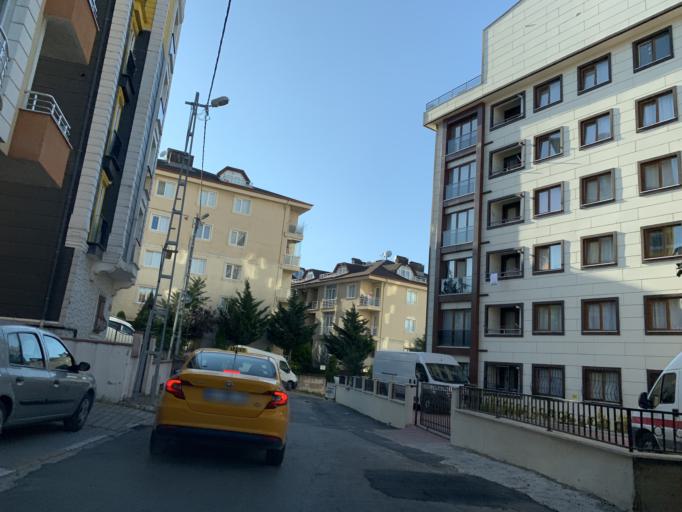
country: TR
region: Istanbul
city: Pendik
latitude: 40.8923
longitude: 29.2550
